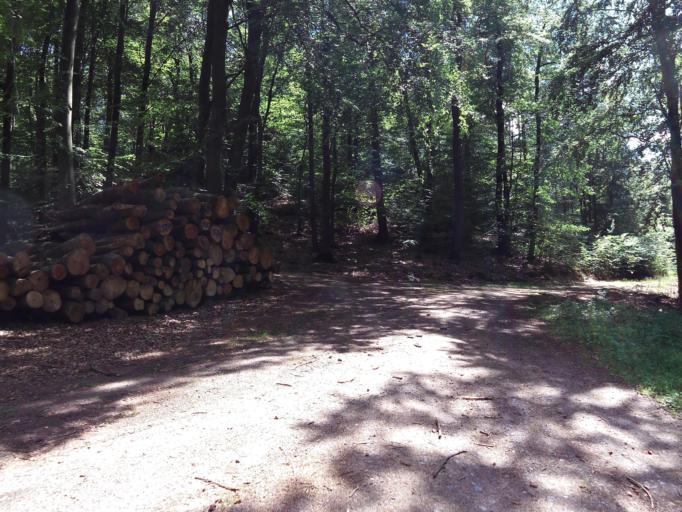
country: DE
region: Rheinland-Pfalz
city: Altleiningen
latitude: 49.4637
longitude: 8.0676
